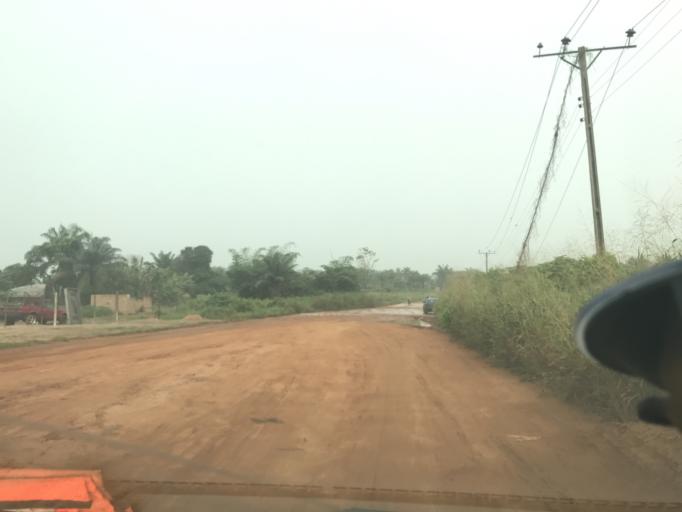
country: NG
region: Ogun
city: Ado Odo
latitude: 6.5552
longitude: 2.9448
